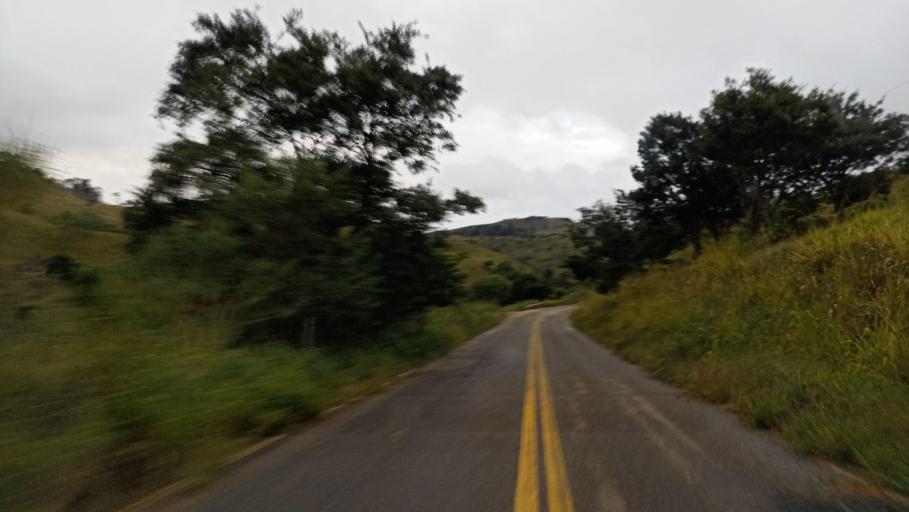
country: BR
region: Bahia
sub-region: Itanhem
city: Itanhem
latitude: -16.6924
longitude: -40.5086
